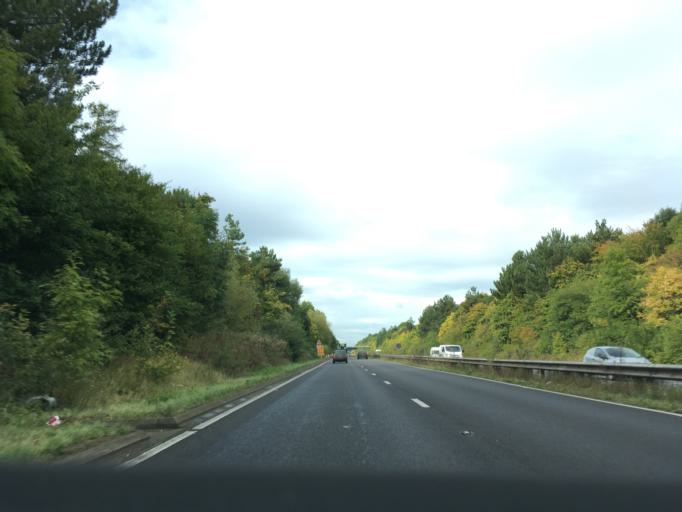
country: GB
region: England
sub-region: Gloucestershire
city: Churchdown
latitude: 51.8845
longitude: -2.1741
